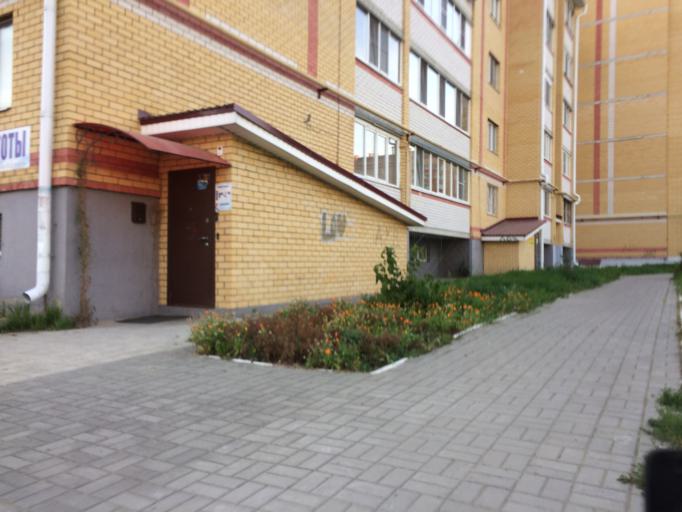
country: RU
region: Mariy-El
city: Yoshkar-Ola
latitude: 56.6282
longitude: 47.8499
